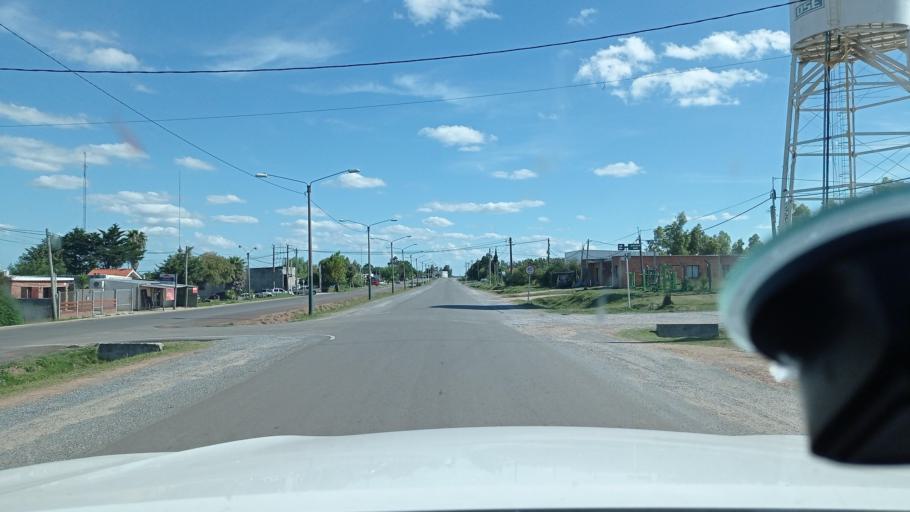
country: UY
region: Florida
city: Florida
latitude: -34.0866
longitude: -56.2375
